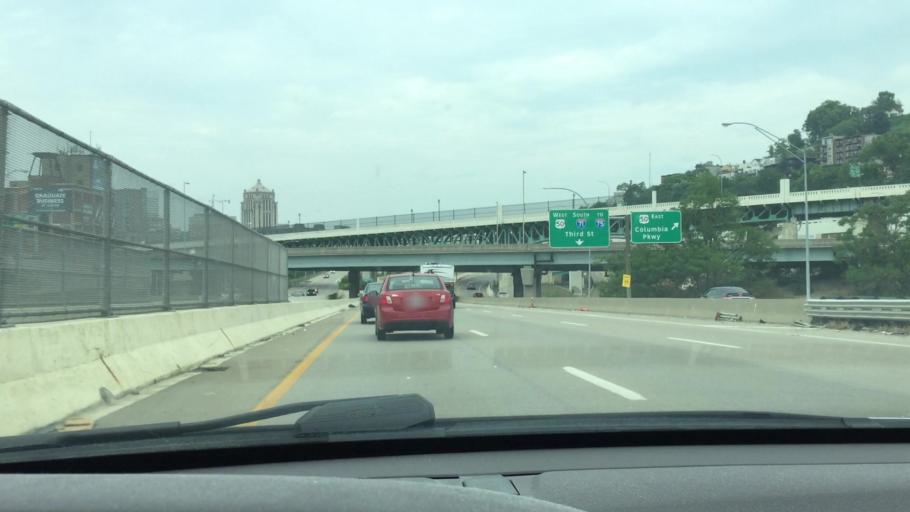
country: US
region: Kentucky
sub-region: Campbell County
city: Newport
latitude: 39.1024
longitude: -84.4981
